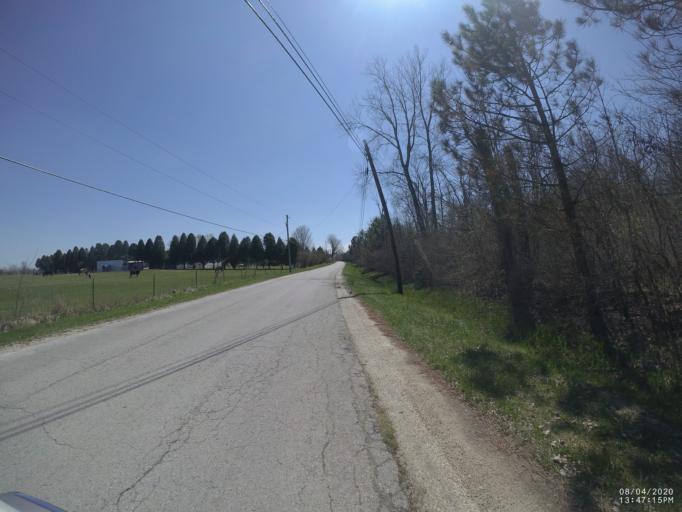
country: US
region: Ohio
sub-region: Sandusky County
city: Gibsonburg
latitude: 41.3183
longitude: -83.2856
